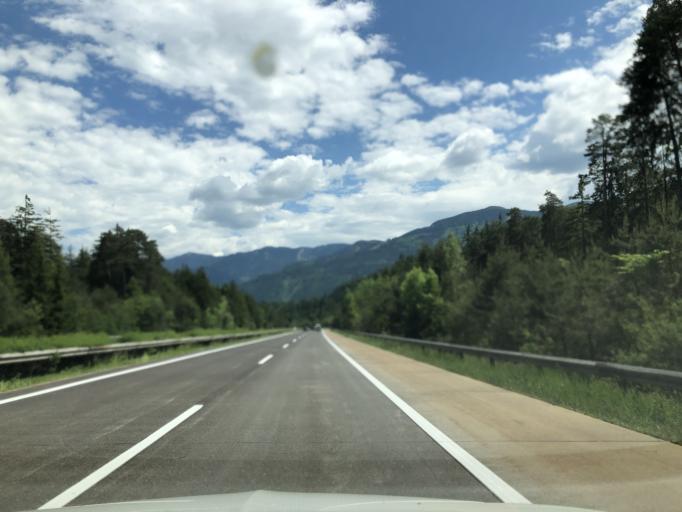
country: AT
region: Carinthia
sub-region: Politischer Bezirk Villach Land
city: Arnoldstein
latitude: 46.5632
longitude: 13.7404
